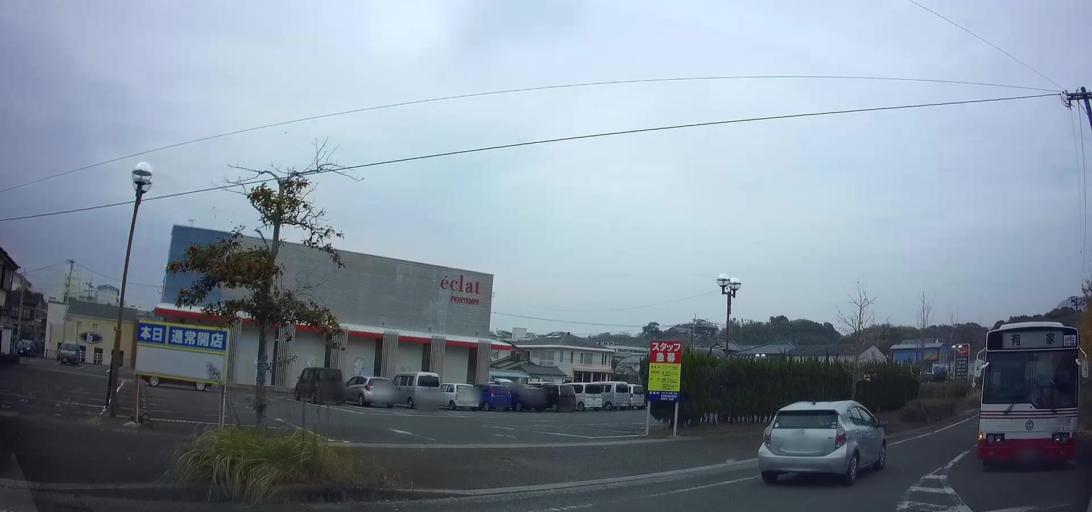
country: JP
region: Nagasaki
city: Shimabara
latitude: 32.6586
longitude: 130.2942
